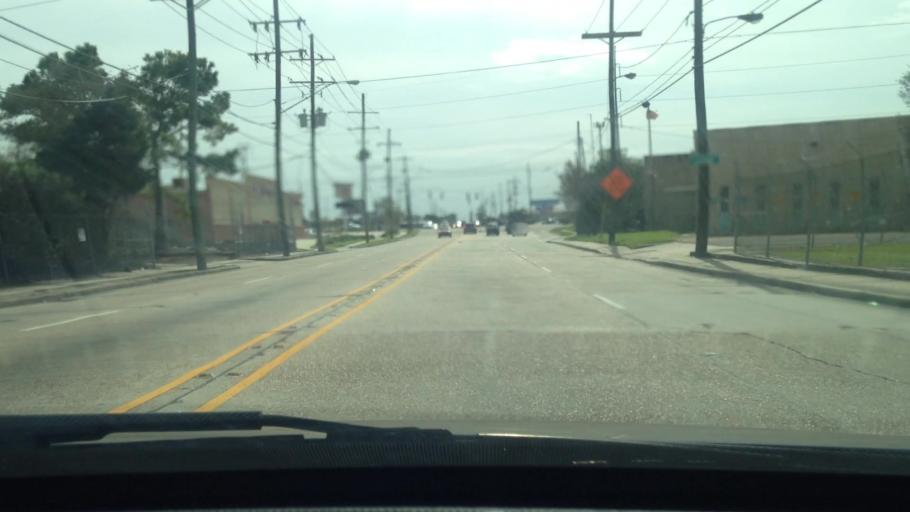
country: US
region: Louisiana
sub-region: Jefferson Parish
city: River Ridge
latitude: 29.9794
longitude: -90.2115
